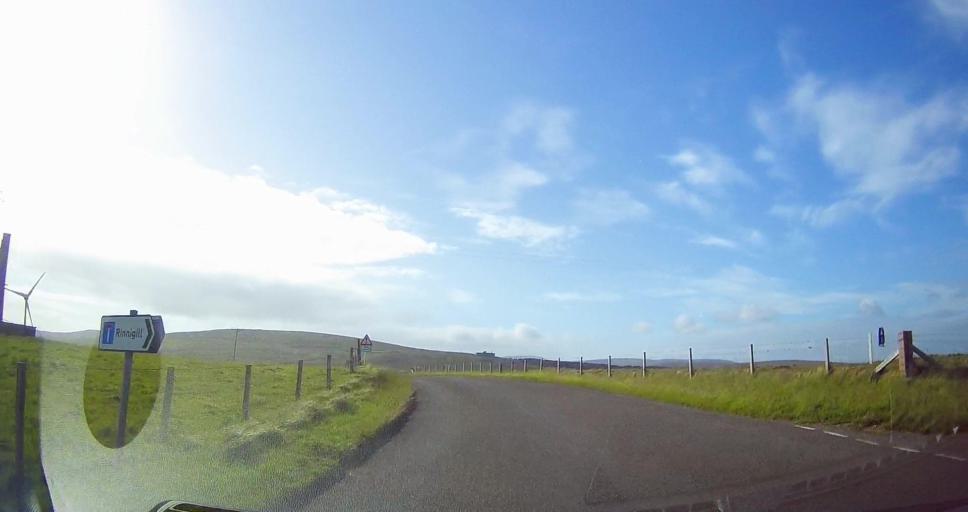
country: GB
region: Scotland
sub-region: Orkney Islands
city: Stromness
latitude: 58.8226
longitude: -3.2065
